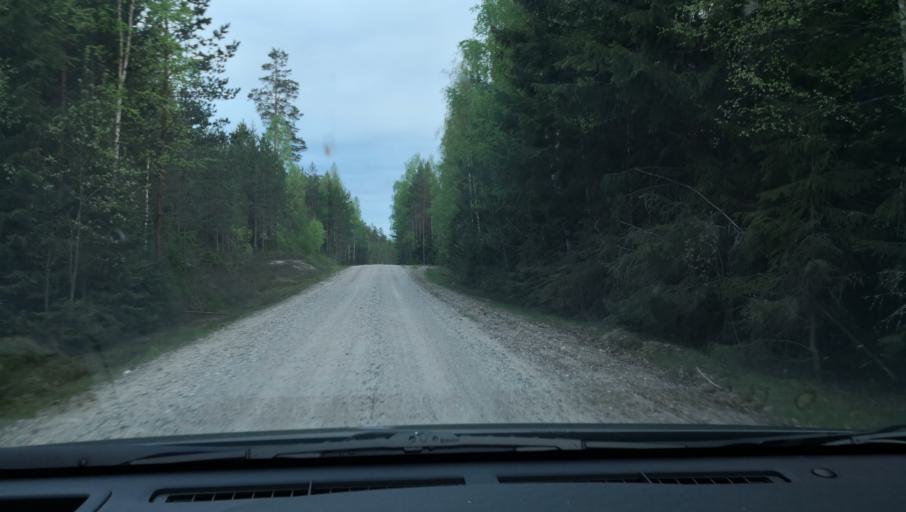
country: SE
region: Vaestmanland
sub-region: Skinnskattebergs Kommun
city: Skinnskatteberg
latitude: 59.7656
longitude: 15.4573
